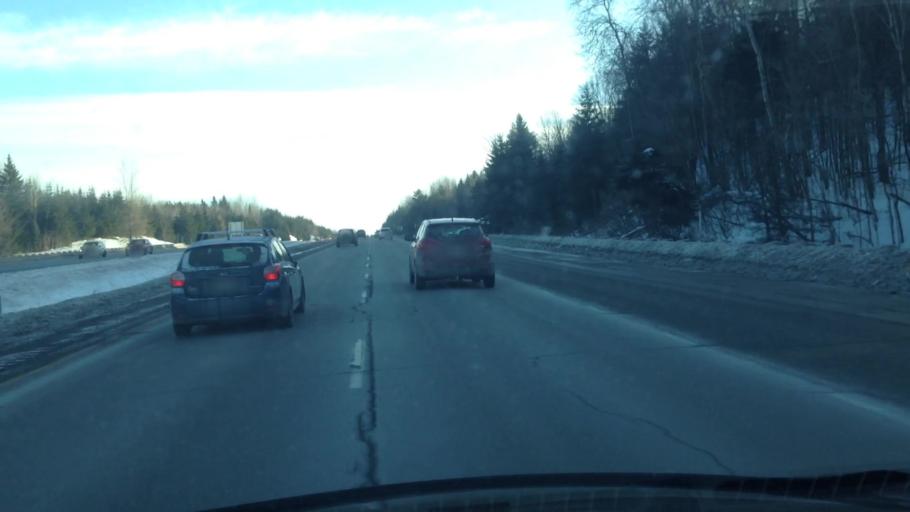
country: CA
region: Quebec
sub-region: Laurentides
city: Prevost
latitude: 45.8627
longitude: -74.0834
